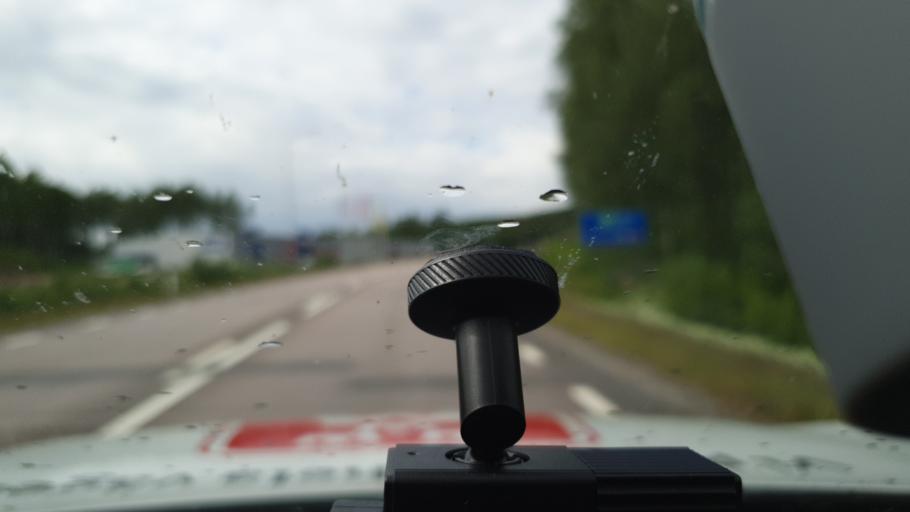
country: SE
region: Vaermland
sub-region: Torsby Kommun
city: Torsby
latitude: 60.1345
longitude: 12.9893
